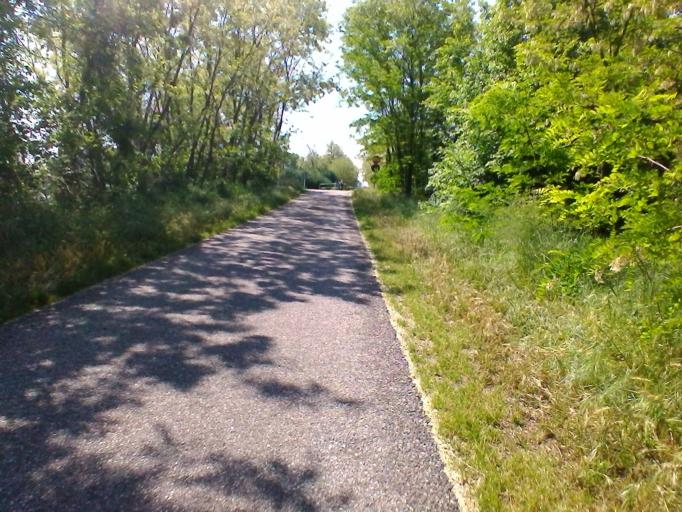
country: IT
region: Lombardy
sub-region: Provincia di Mantova
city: Soave
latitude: 45.2020
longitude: 10.7123
